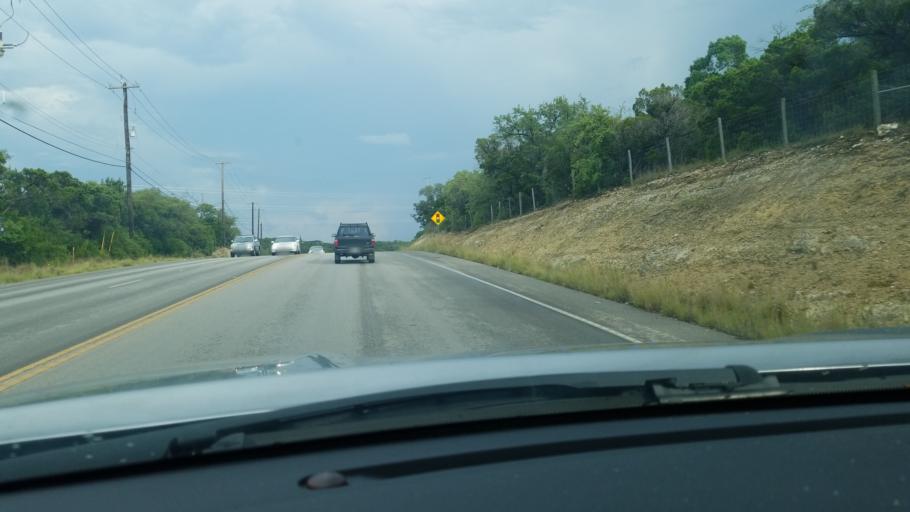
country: US
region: Texas
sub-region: Bexar County
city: Timberwood Park
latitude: 29.7124
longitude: -98.4510
